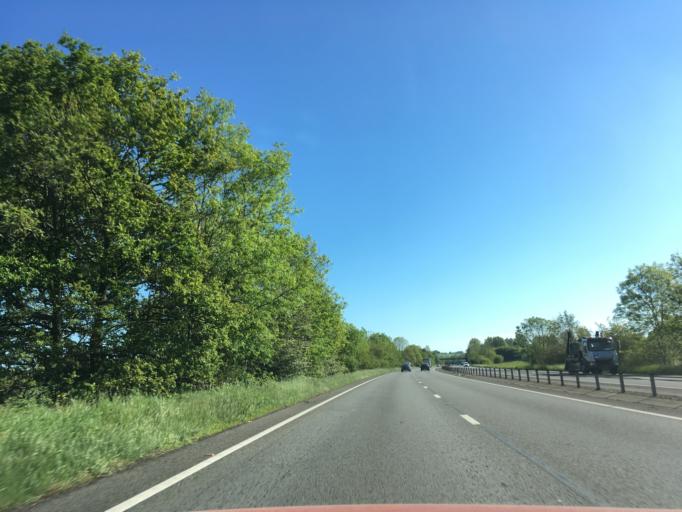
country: GB
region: Wales
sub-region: Monmouthshire
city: Llangwm
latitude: 51.7228
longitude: -2.8557
